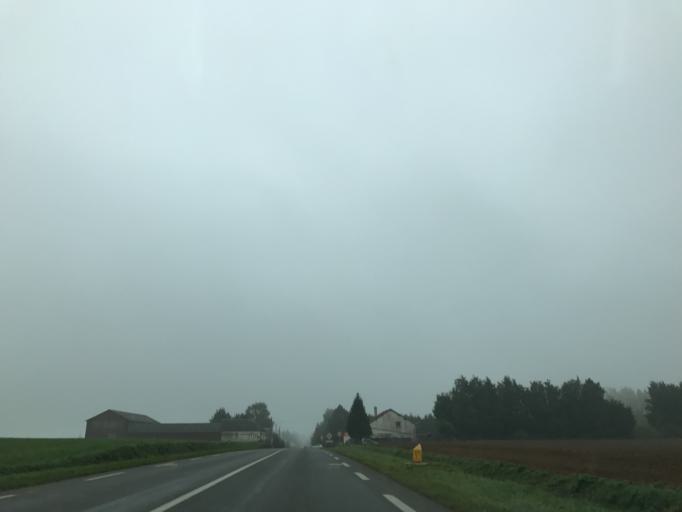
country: FR
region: Nord-Pas-de-Calais
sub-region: Departement du Pas-de-Calais
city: Bapaume
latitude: 50.0690
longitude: 2.8880
